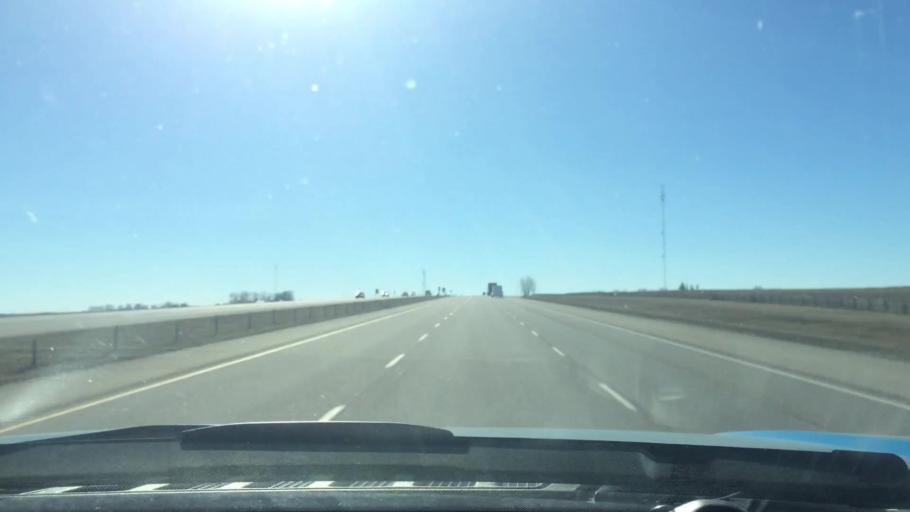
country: CA
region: Alberta
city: Crossfield
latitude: 51.4267
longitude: -114.0021
